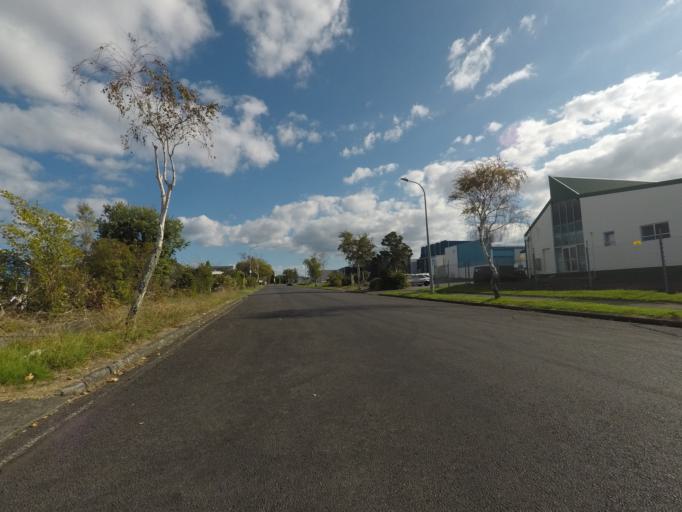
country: NZ
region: Auckland
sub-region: Auckland
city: Rosebank
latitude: -36.8841
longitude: 174.6860
